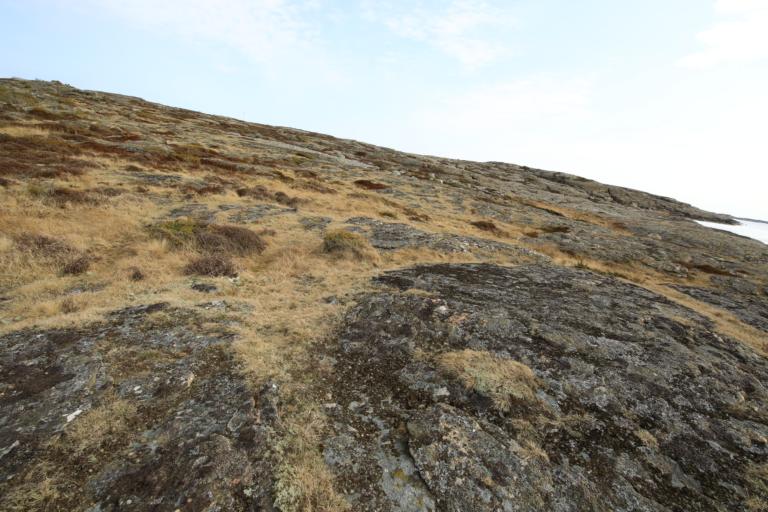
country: SE
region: Halland
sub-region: Kungsbacka Kommun
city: Frillesas
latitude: 57.2542
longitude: 12.0896
